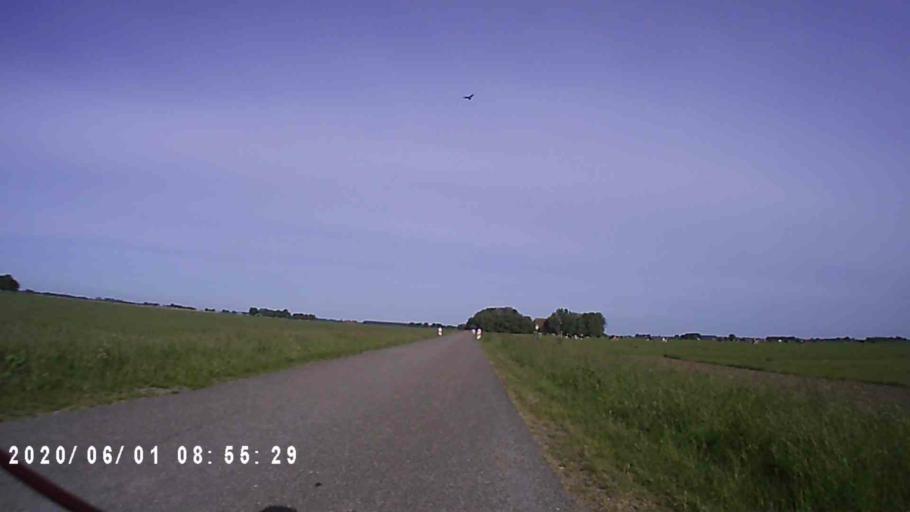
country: NL
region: Friesland
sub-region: Gemeente Leeuwarderadeel
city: Britsum
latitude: 53.2784
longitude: 5.8242
